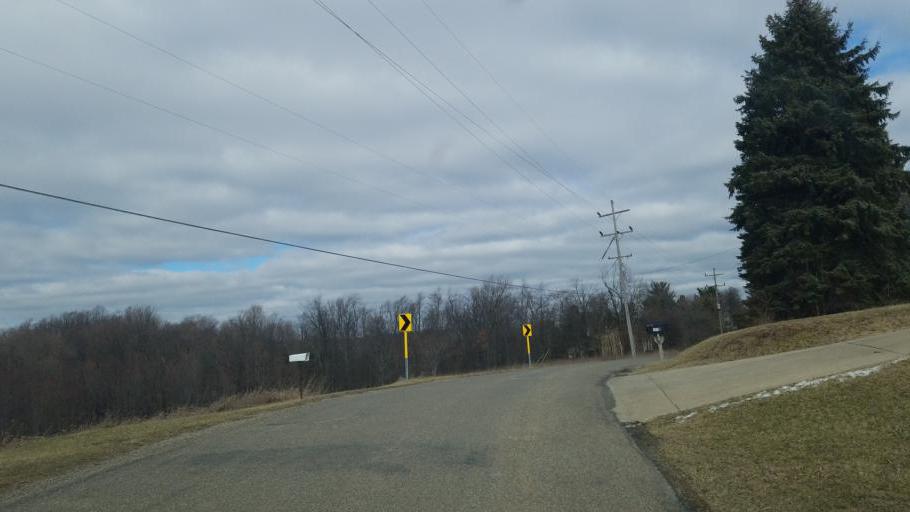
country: US
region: Ohio
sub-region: Sandusky County
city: Bellville
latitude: 40.6649
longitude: -82.5120
